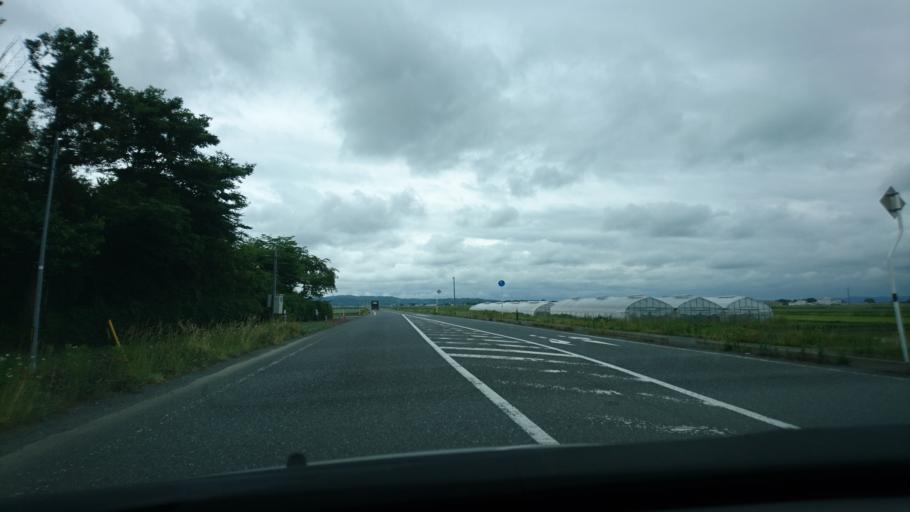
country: JP
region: Miyagi
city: Wakuya
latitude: 38.6953
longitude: 141.2604
